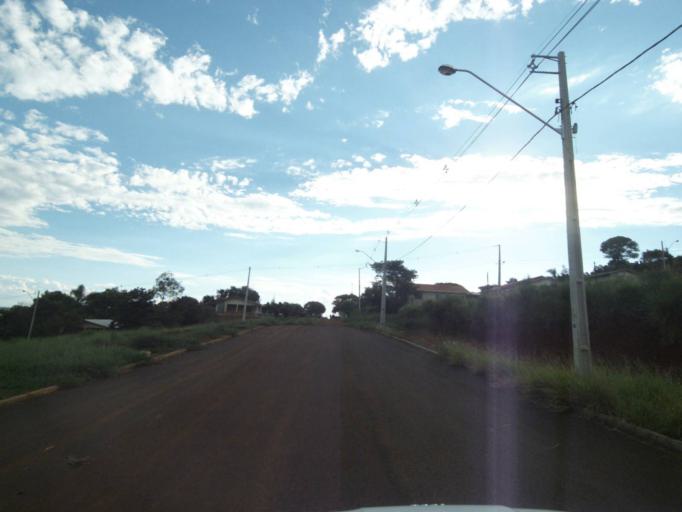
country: BR
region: Parana
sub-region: Laranjeiras Do Sul
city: Laranjeiras do Sul
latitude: -25.4906
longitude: -52.5234
